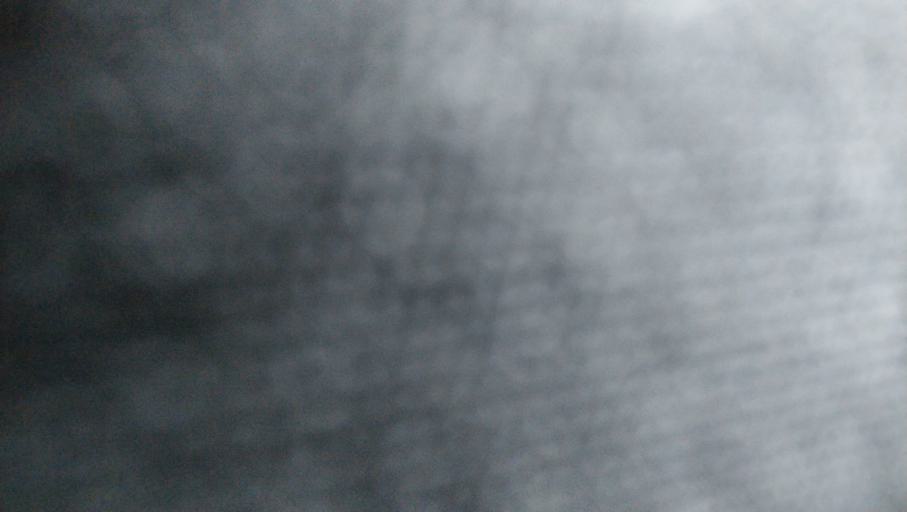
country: MX
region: Oaxaca
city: Juchitan de Zaragoza
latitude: 16.4436
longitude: -95.0211
